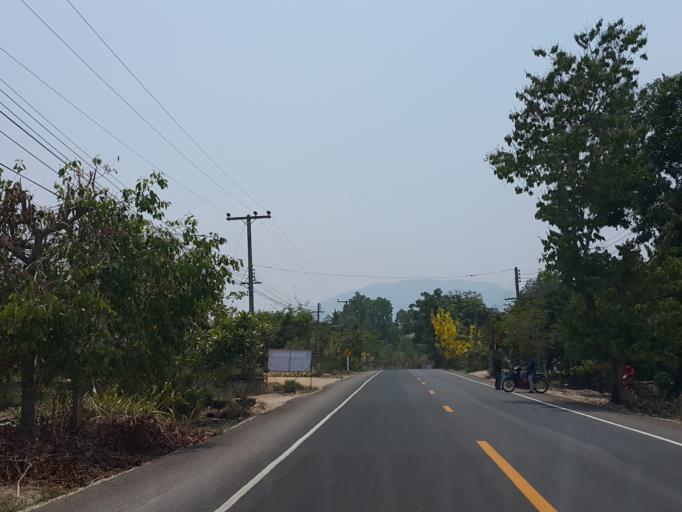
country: TH
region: Kamphaeng Phet
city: Pang Sila Thong
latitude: 16.0281
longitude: 99.3716
